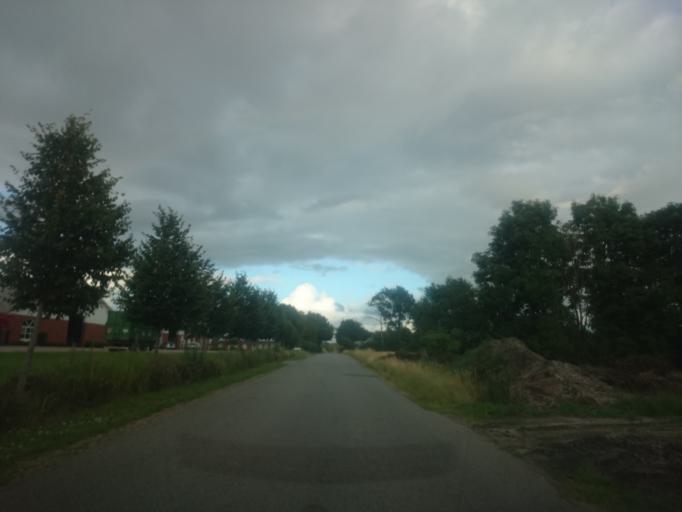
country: DK
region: South Denmark
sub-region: Billund Kommune
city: Grindsted
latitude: 55.6480
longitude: 8.8367
